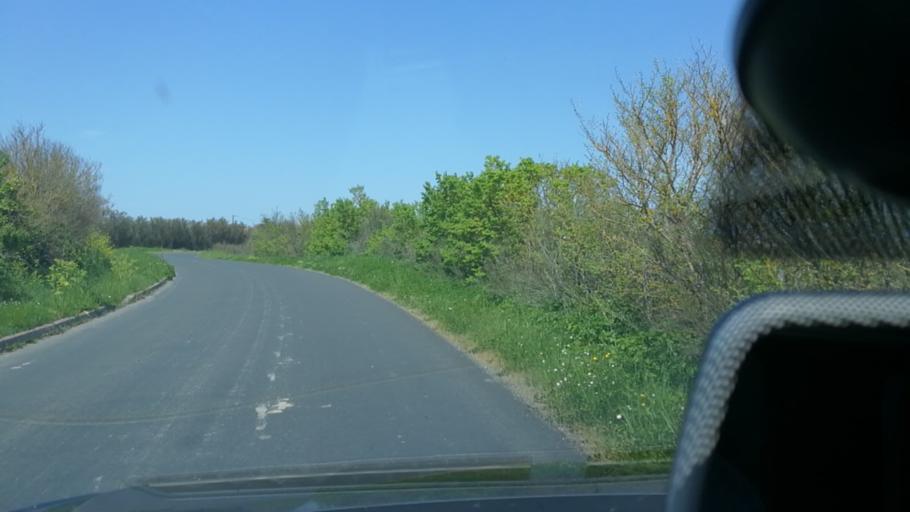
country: FR
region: Poitou-Charentes
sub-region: Departement de la Charente-Maritime
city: Saint-Trojan-les-Bains
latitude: 45.8785
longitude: -1.1991
